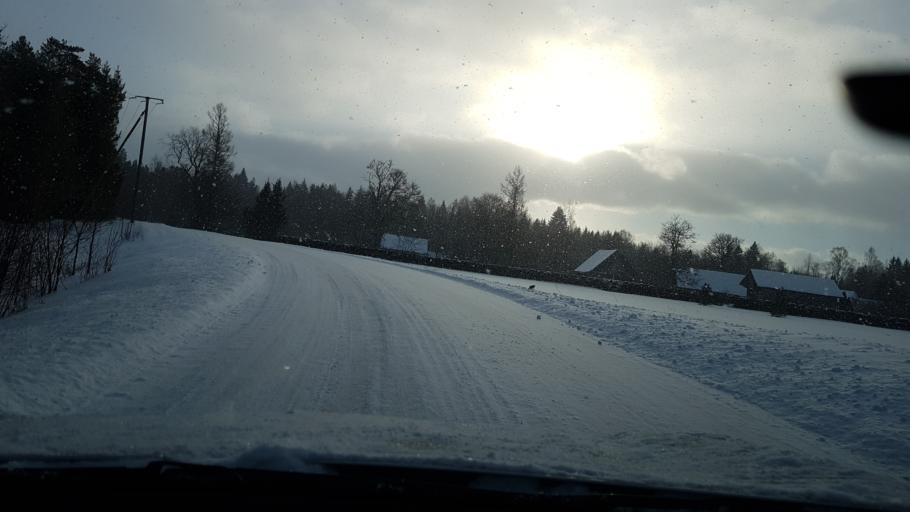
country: EE
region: Harju
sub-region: Nissi vald
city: Turba
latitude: 59.1881
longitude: 24.1393
